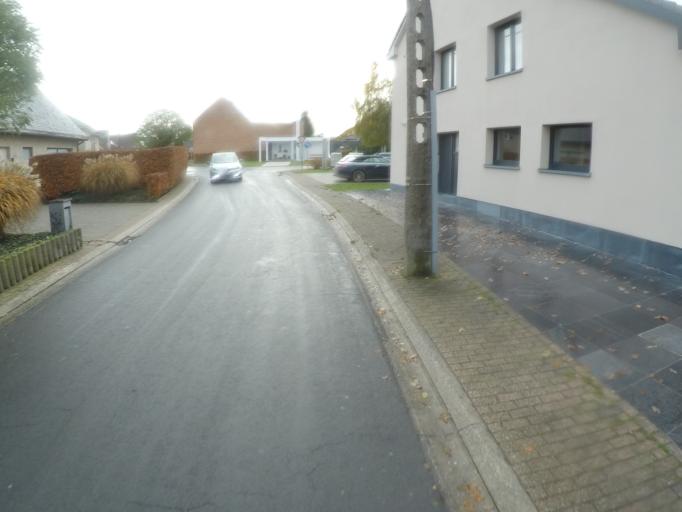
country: BE
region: Flanders
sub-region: Provincie Vlaams-Brabant
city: Opwijk
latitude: 50.9655
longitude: 4.1917
